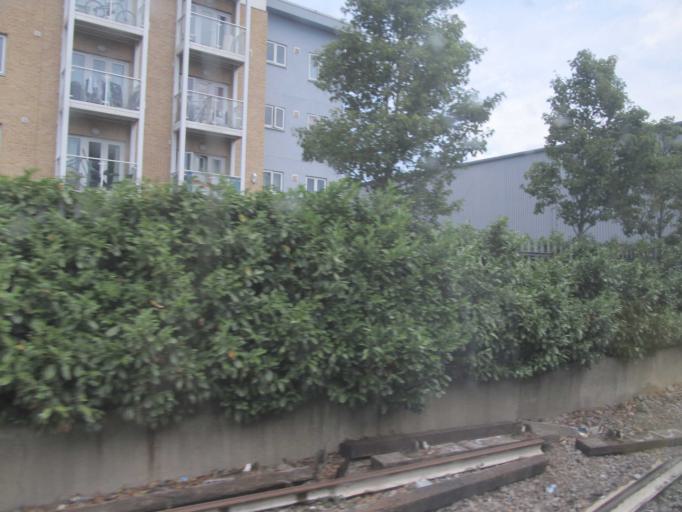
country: GB
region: England
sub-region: Slough
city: Slough
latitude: 51.5130
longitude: -0.5905
